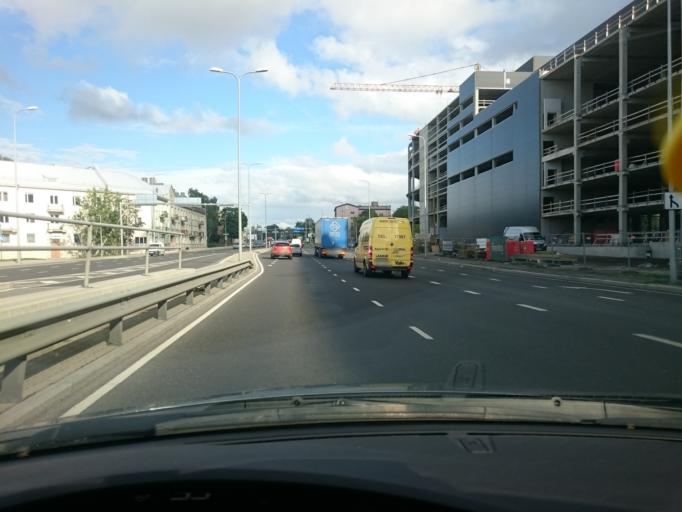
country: EE
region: Harju
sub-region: Tallinna linn
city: Tallinn
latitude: 59.4249
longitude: 24.7931
